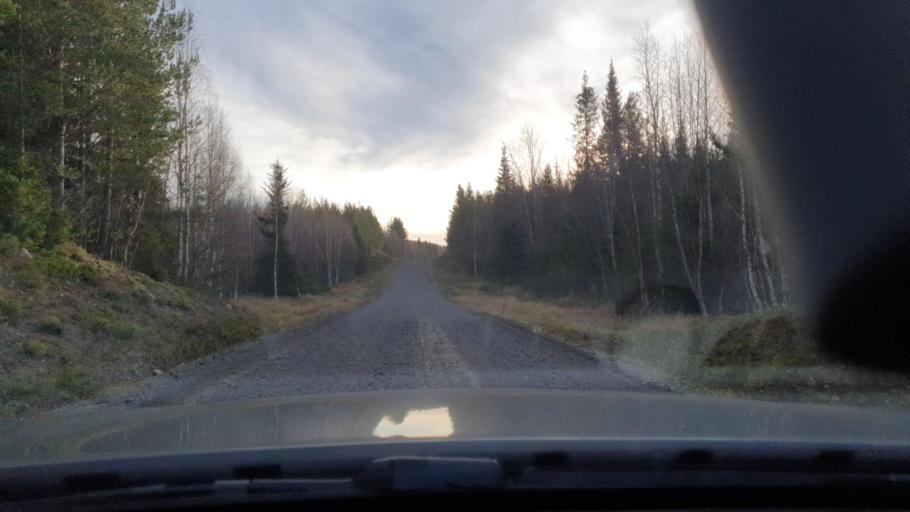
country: SE
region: Jaemtland
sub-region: Stroemsunds Kommun
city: Stroemsund
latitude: 63.5408
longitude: 15.5832
